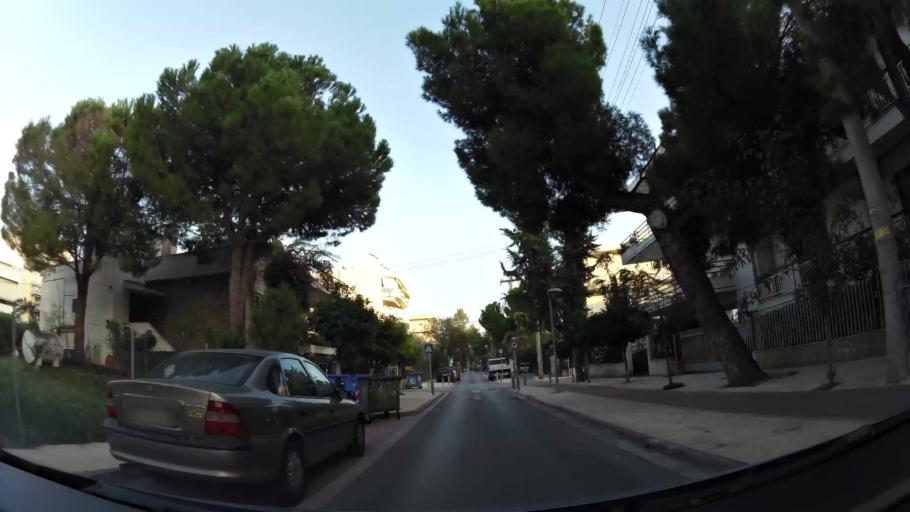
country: GR
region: Attica
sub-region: Nomarchia Athinas
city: Agia Paraskevi
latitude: 38.0210
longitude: 23.8271
